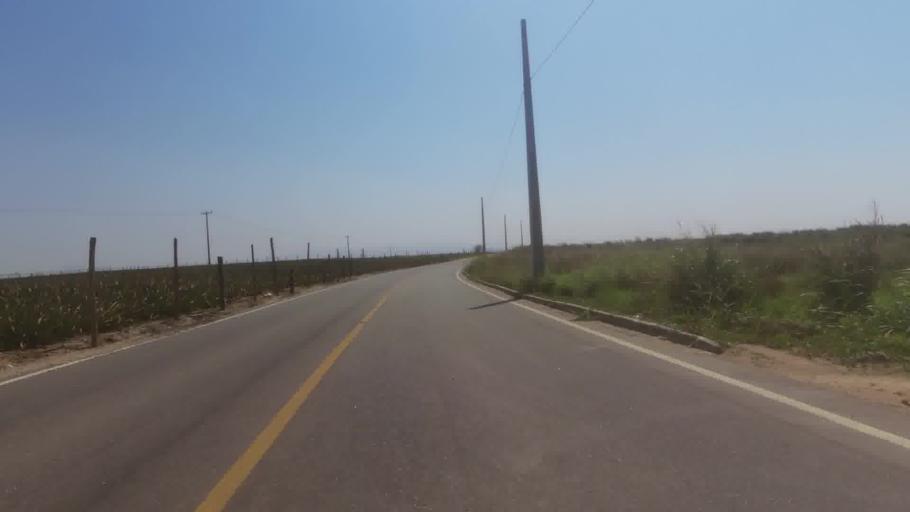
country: BR
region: Espirito Santo
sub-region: Itapemirim
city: Itapemirim
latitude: -21.0267
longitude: -40.8384
